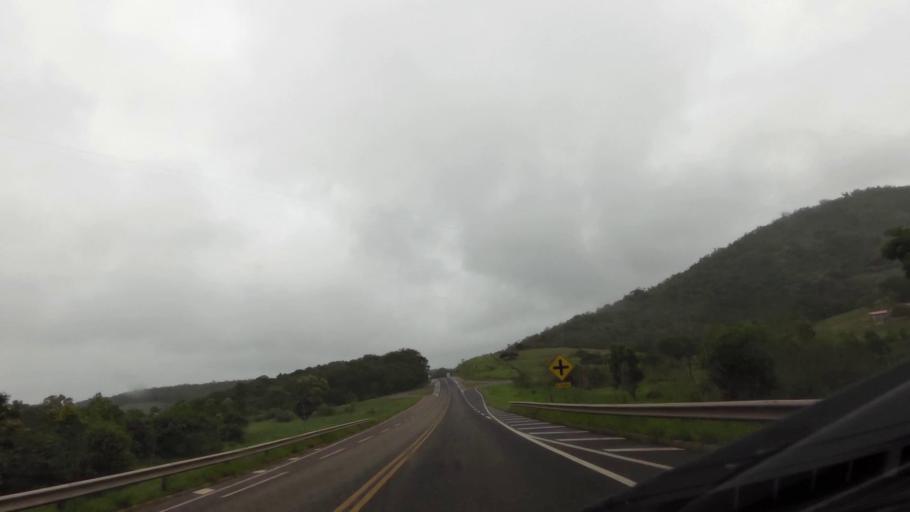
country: BR
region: Espirito Santo
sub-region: Guarapari
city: Guarapari
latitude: -20.7233
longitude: -40.5718
